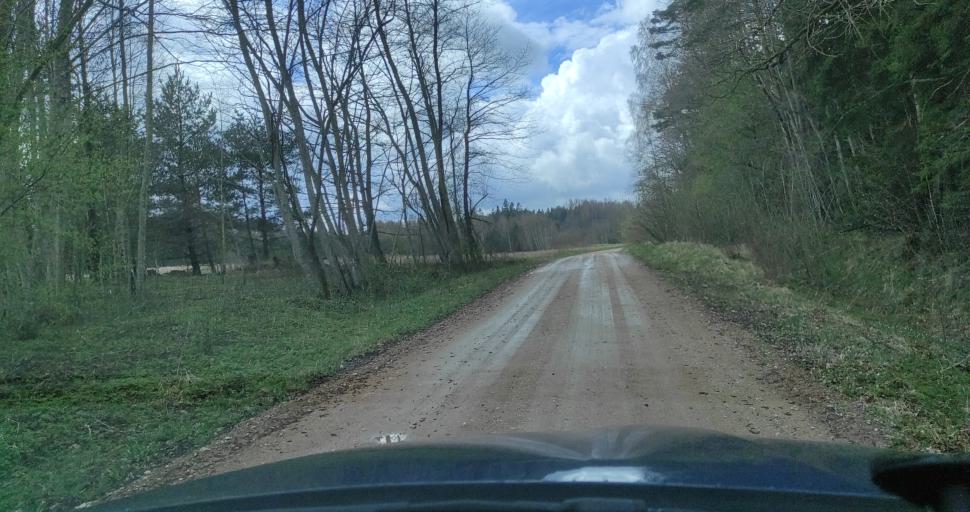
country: LV
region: Kuldigas Rajons
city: Kuldiga
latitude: 57.0574
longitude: 21.8022
